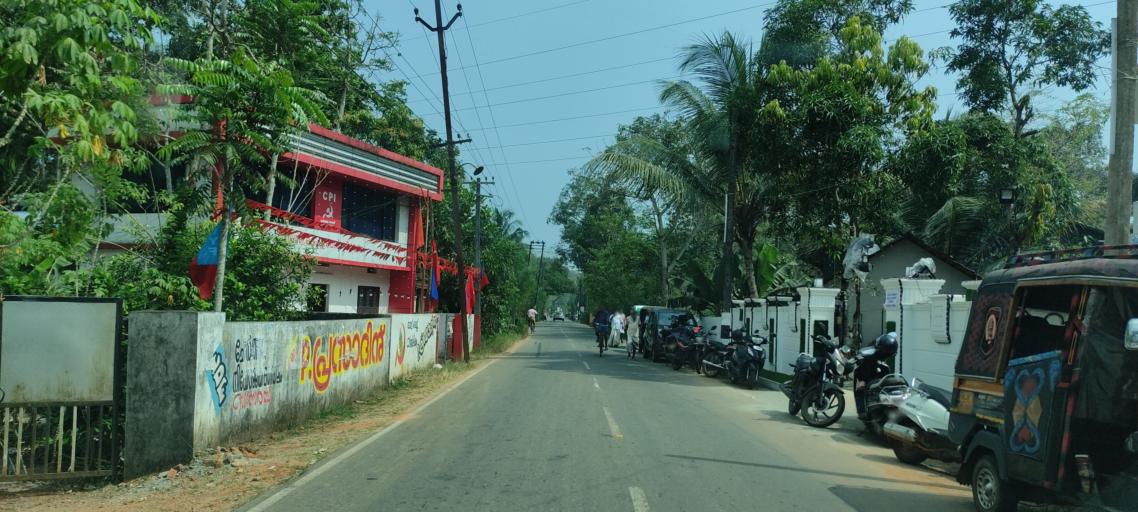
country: IN
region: Kerala
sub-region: Alappuzha
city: Shertallai
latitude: 9.6547
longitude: 76.3485
